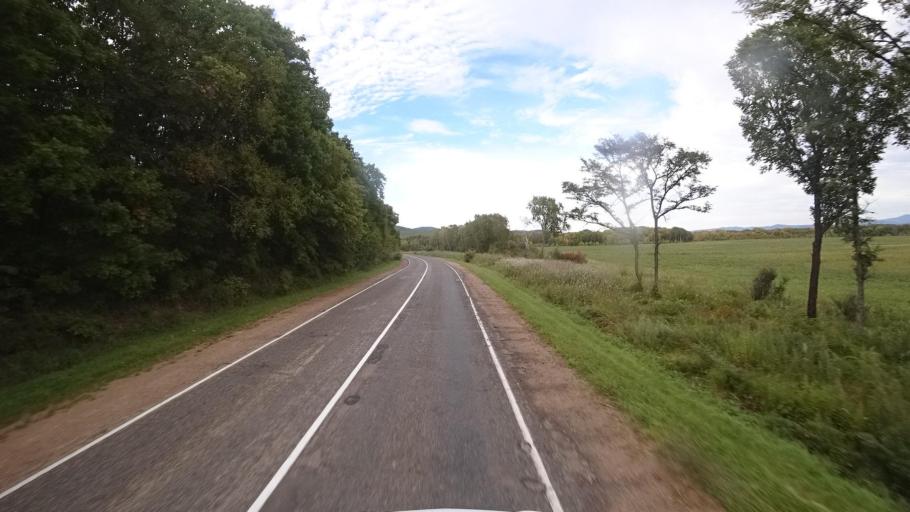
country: RU
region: Primorskiy
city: Dostoyevka
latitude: 44.3619
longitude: 133.4317
